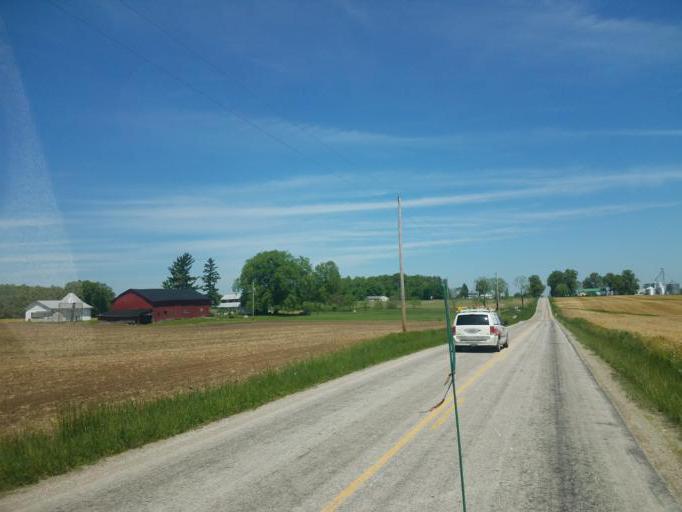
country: US
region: Ohio
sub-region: Ashland County
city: Ashland
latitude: 40.9169
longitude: -82.2432
